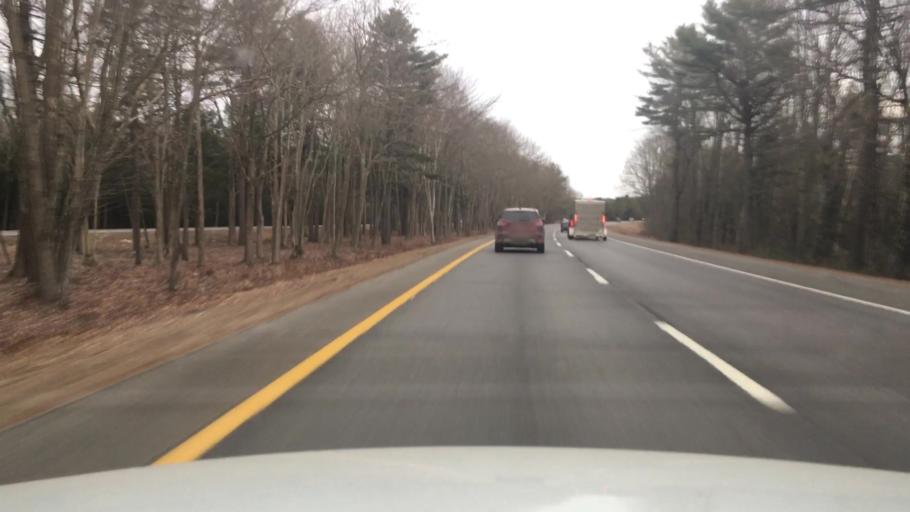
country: US
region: Maine
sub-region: Sagadahoc County
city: Bath
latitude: 43.9174
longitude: -69.8921
